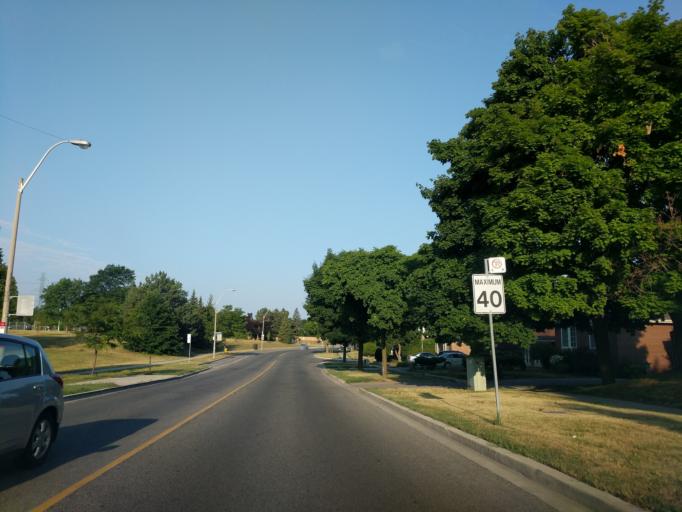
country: CA
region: Ontario
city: Willowdale
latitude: 43.8000
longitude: -79.3517
